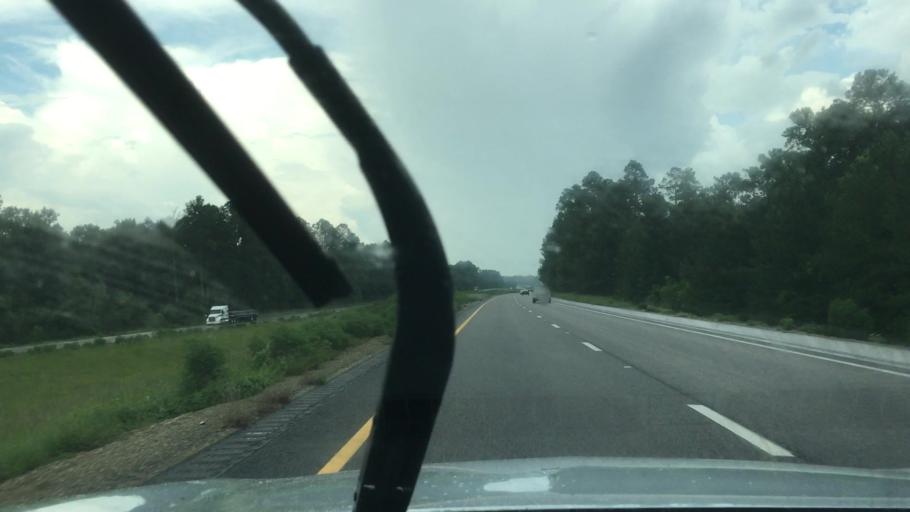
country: US
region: Mississippi
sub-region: Lamar County
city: Purvis
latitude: 31.2063
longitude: -89.3346
